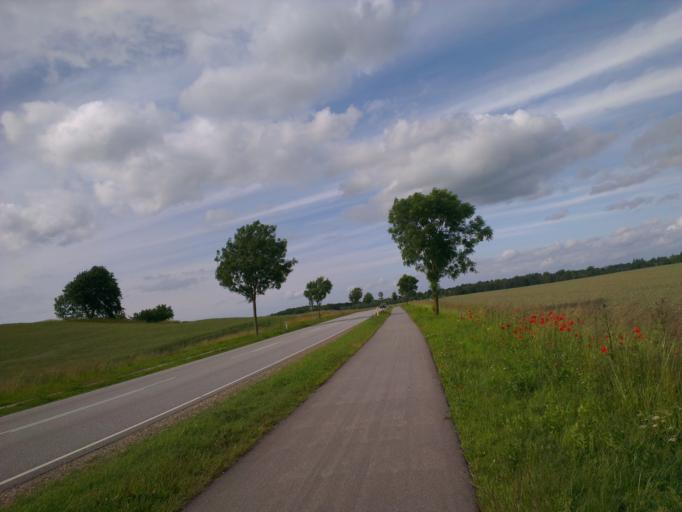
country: DK
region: Capital Region
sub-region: Frederikssund Kommune
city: Skibby
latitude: 55.7299
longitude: 11.9456
